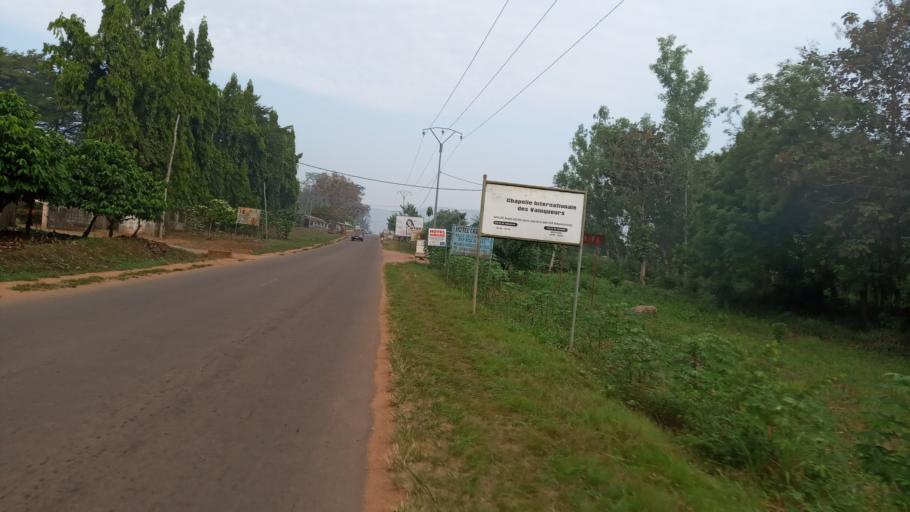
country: TG
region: Plateaux
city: Kpalime
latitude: 6.8890
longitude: 0.6428
